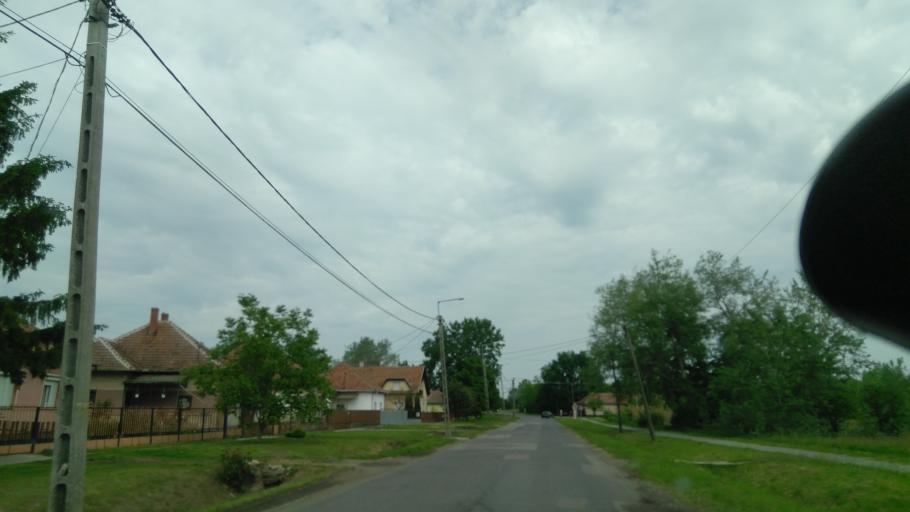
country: HU
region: Bekes
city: Szeghalom
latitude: 47.0317
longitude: 21.1660
